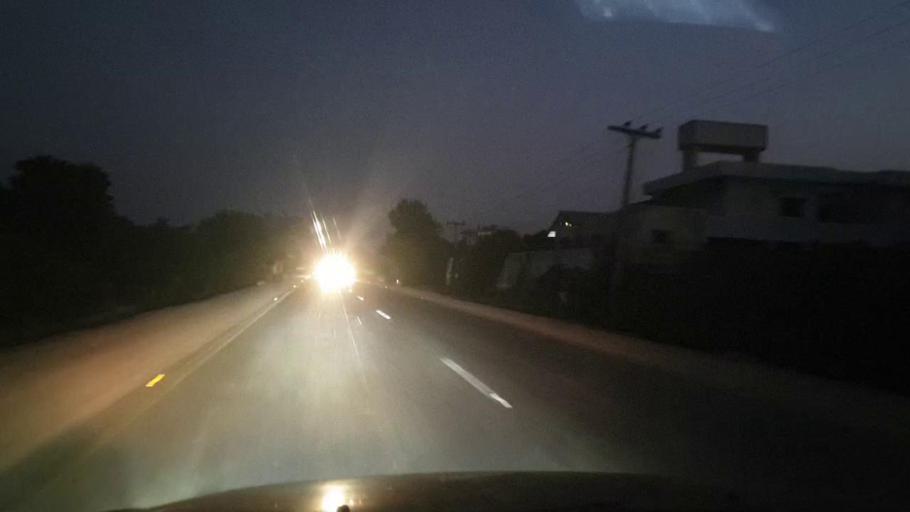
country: PK
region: Sindh
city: Chambar
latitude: 25.3221
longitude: 68.8018
